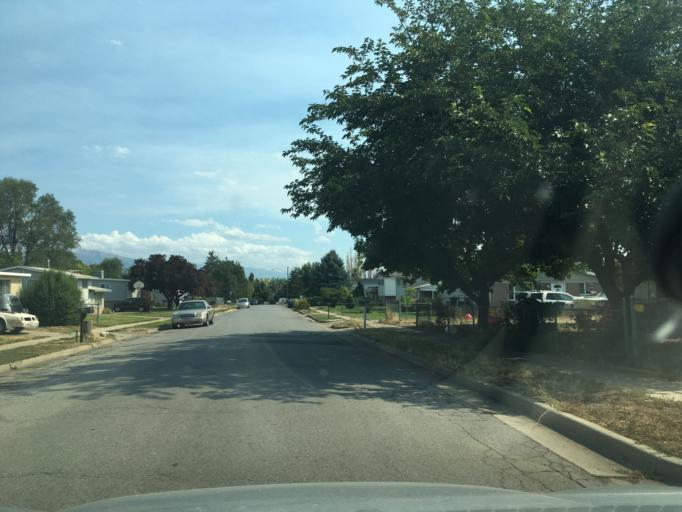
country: US
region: Utah
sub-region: Davis County
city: Clearfield
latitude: 41.0851
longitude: -112.0058
